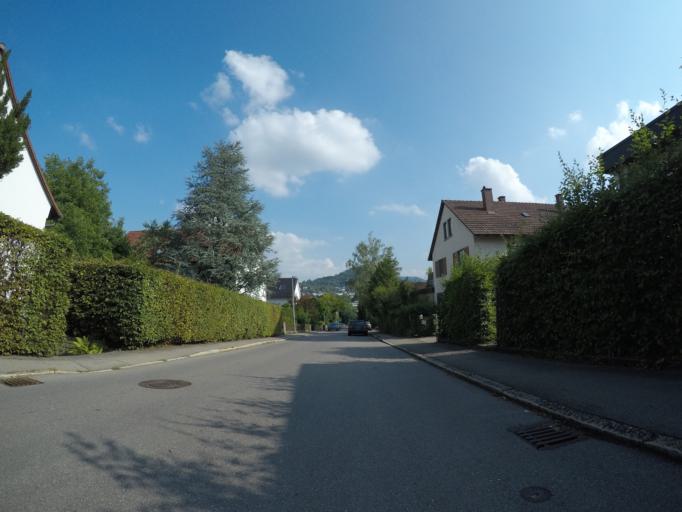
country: DE
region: Baden-Wuerttemberg
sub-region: Tuebingen Region
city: Reutlingen
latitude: 48.4848
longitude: 9.2002
